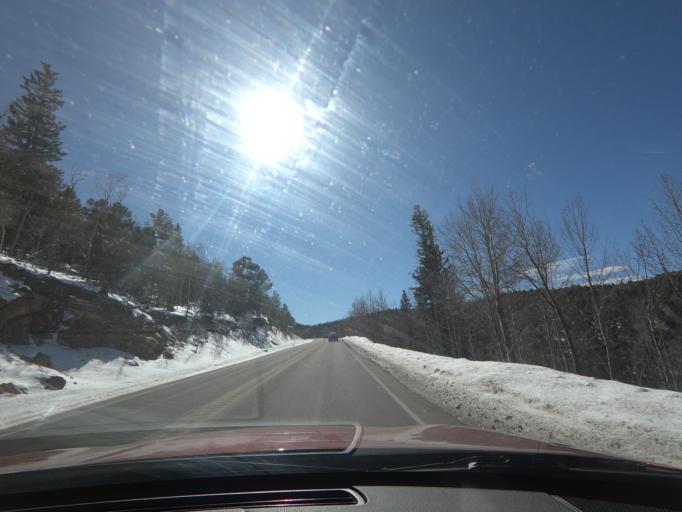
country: US
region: Colorado
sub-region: Teller County
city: Cripple Creek
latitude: 38.8088
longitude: -105.1247
